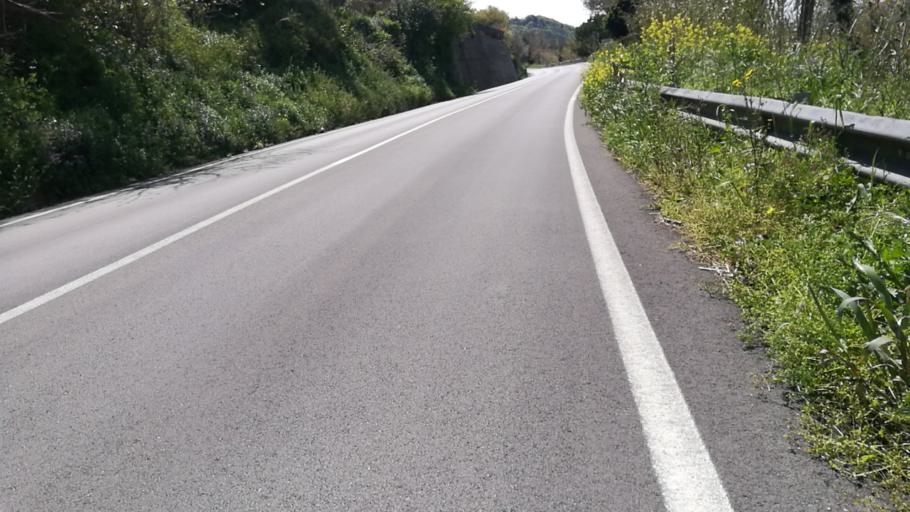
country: IT
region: Abruzzo
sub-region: Provincia di Chieti
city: Marina di San Vito
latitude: 42.3022
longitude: 14.4424
